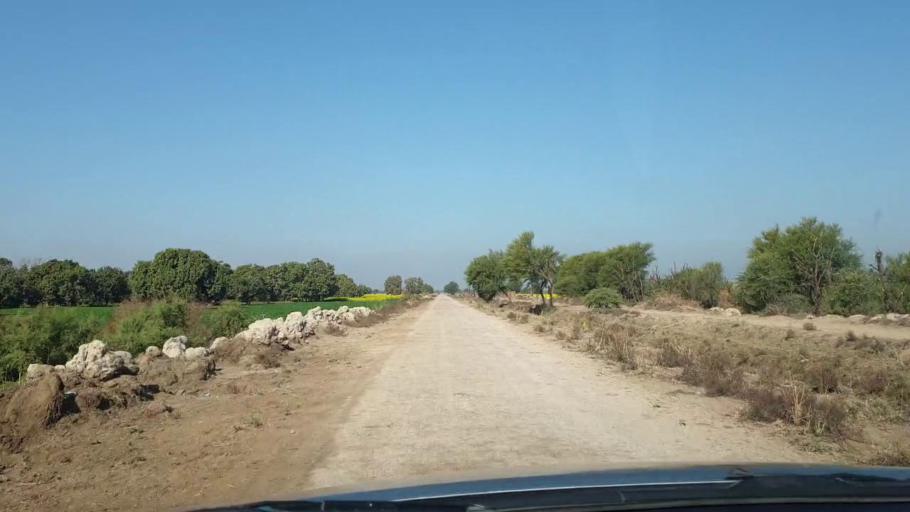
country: PK
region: Sindh
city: Jhol
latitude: 25.8826
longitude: 68.9013
